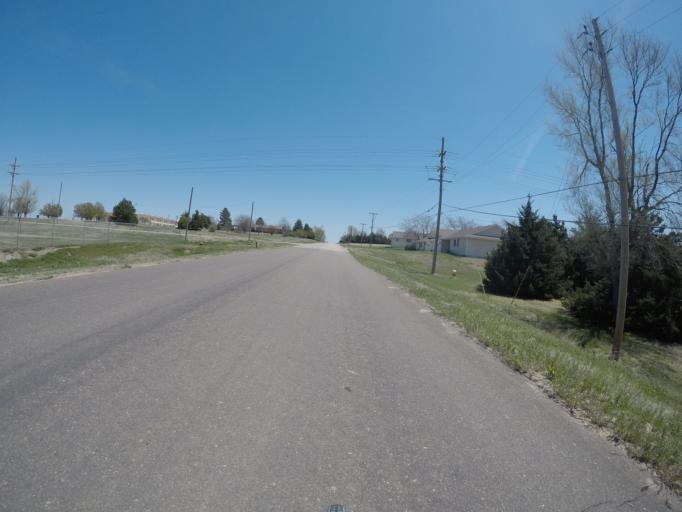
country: US
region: Kansas
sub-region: Pratt County
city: Pratt
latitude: 37.6420
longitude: -98.7581
